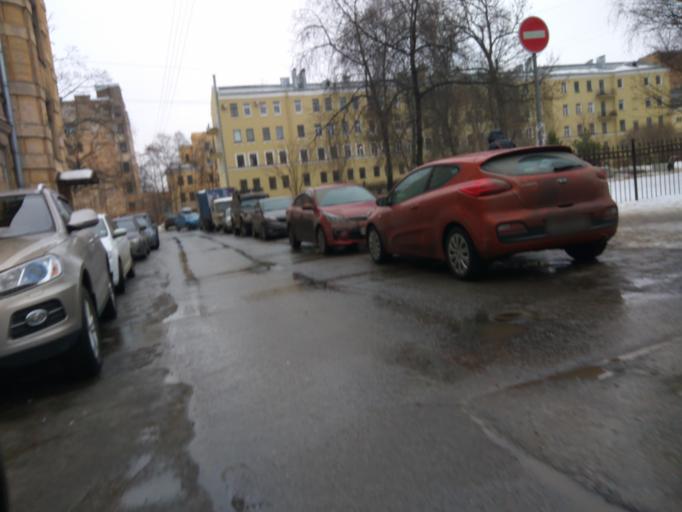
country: RU
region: St.-Petersburg
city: Centralniy
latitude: 59.9445
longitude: 30.3810
